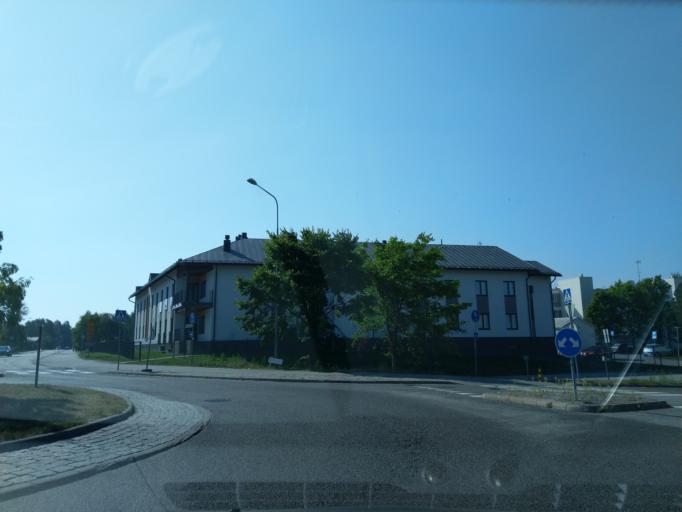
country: FI
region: Satakunta
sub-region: Pori
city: Noormarkku
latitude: 61.5928
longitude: 21.8683
